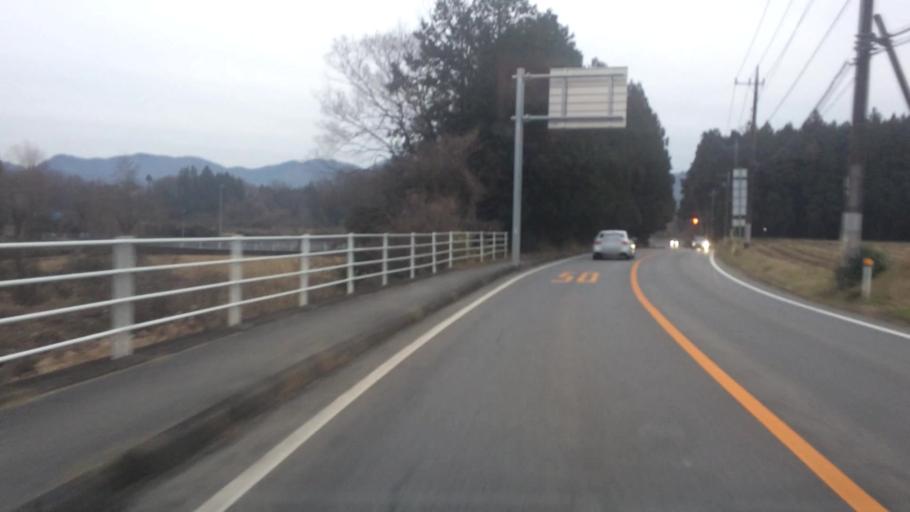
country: JP
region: Tochigi
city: Imaichi
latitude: 36.6693
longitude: 139.7751
